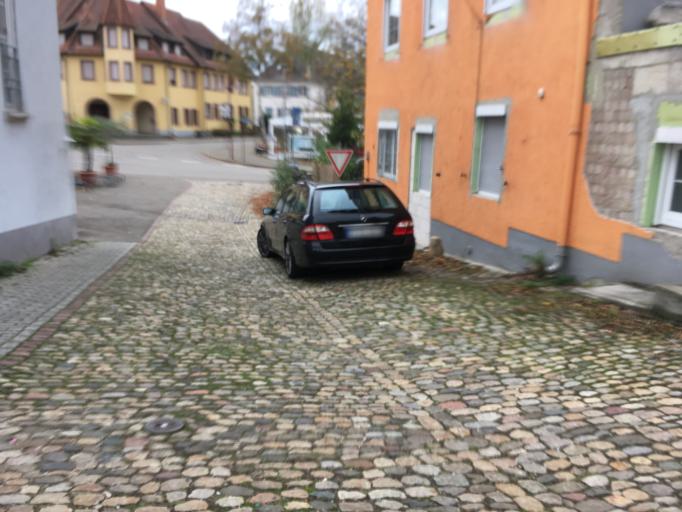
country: DE
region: Baden-Wuerttemberg
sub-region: Freiburg Region
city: Breisach am Rhein
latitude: 48.0284
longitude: 7.5803
